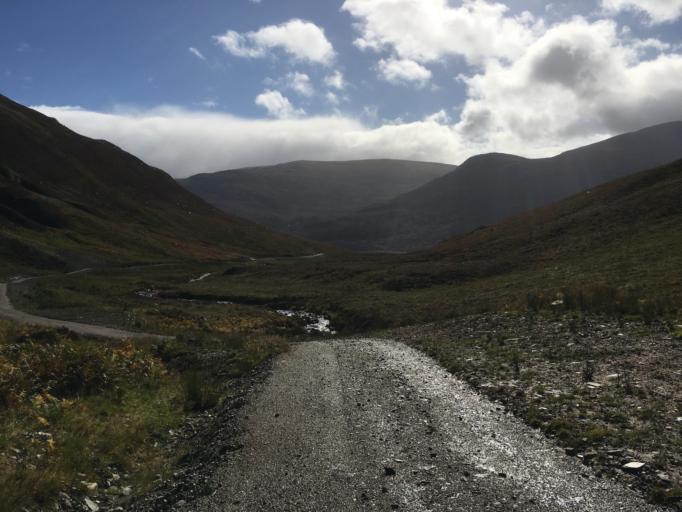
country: GB
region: Scotland
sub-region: Highland
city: Spean Bridge
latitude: 57.3516
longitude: -4.9865
